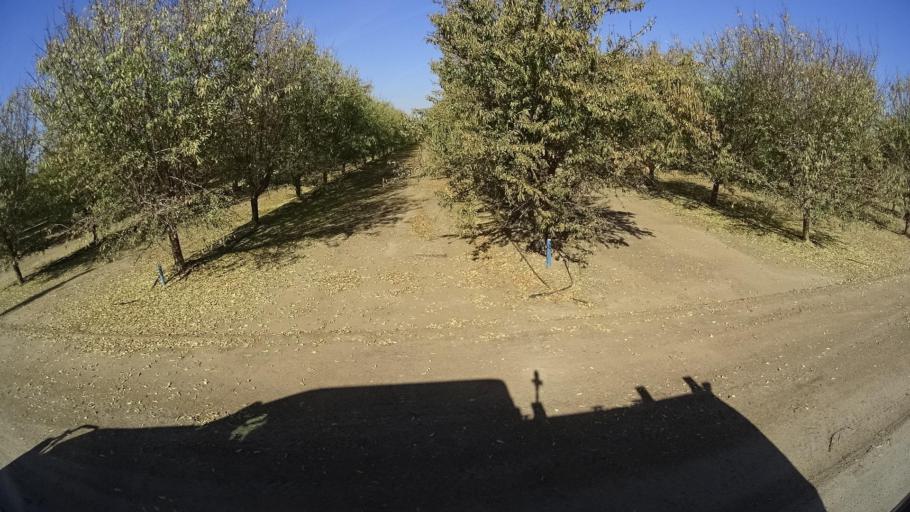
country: US
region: California
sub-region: Kern County
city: McFarland
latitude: 35.6456
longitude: -119.2022
